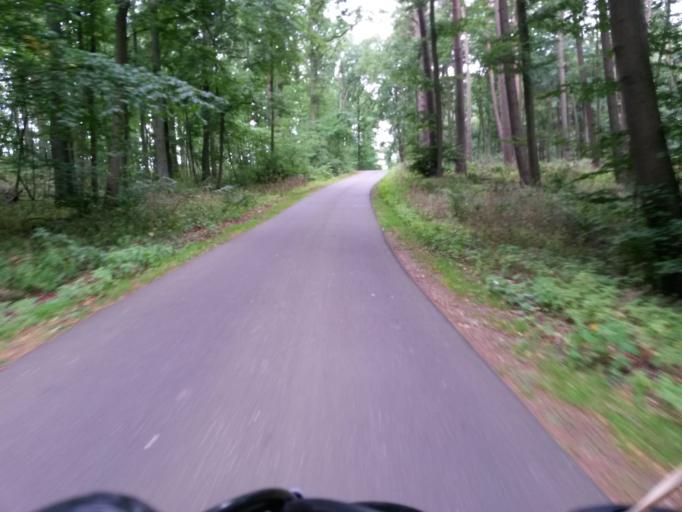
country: DE
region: Brandenburg
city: Angermunde
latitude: 53.0599
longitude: 13.9360
